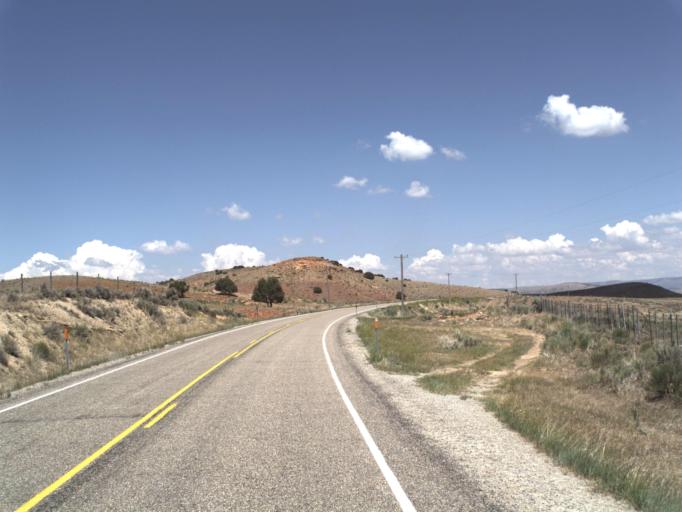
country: US
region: Utah
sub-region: Rich County
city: Randolph
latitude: 41.5150
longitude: -111.2133
